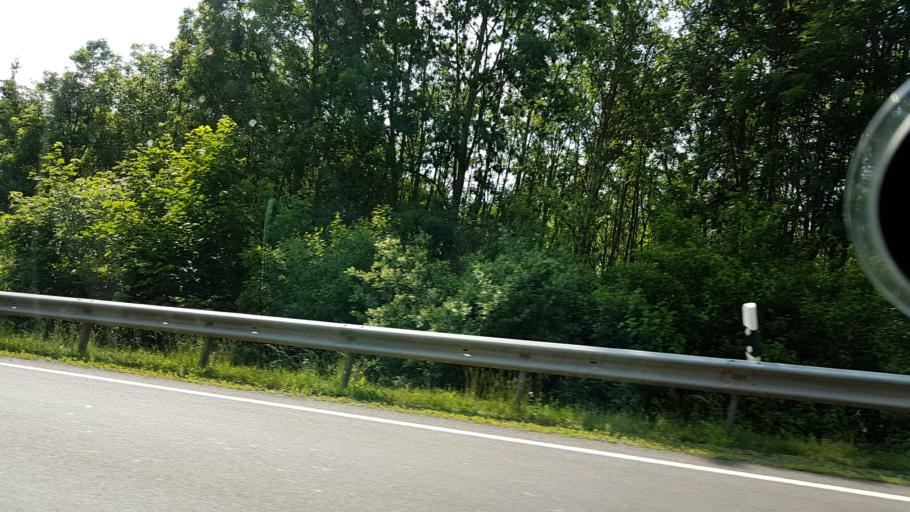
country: DE
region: Rheinland-Pfalz
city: Mettweiler
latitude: 49.5926
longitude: 7.3006
